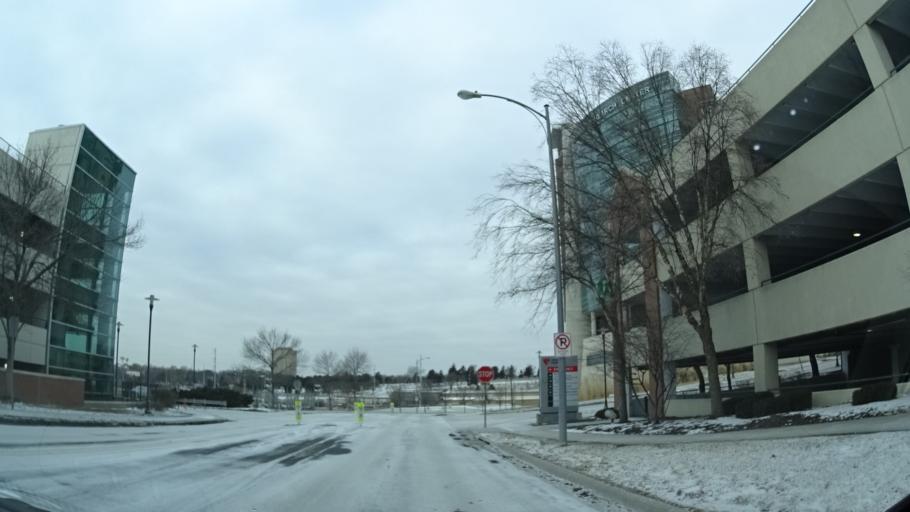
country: US
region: Nebraska
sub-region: Douglas County
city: Omaha
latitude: 41.2543
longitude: -95.9799
